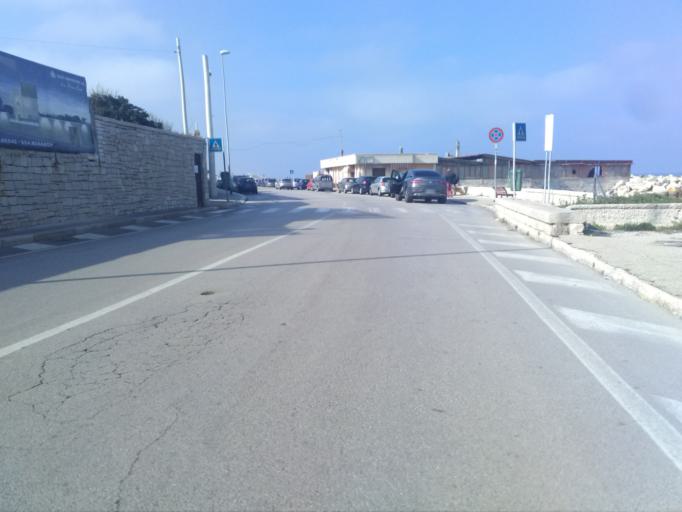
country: IT
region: Apulia
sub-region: Provincia di Bari
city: San Paolo
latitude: 41.1642
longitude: 16.7564
